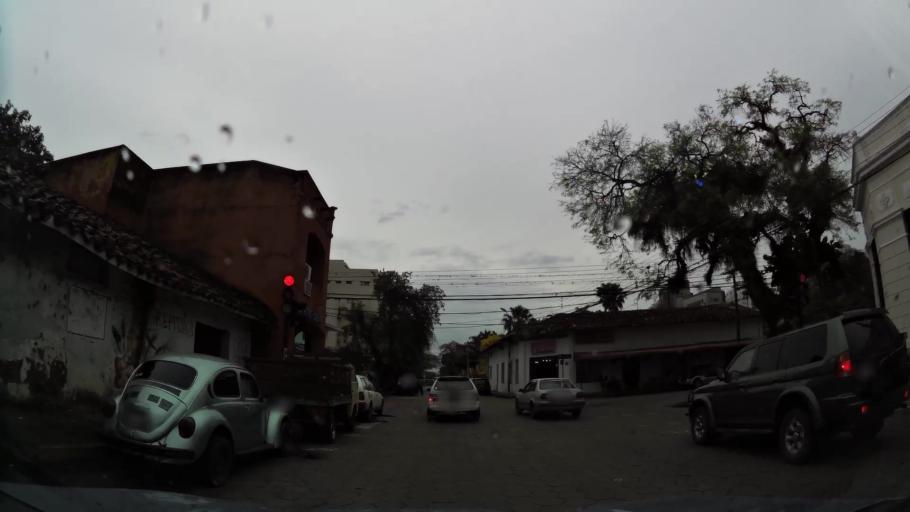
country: BO
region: Santa Cruz
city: Santa Cruz de la Sierra
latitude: -17.7897
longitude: -63.1801
